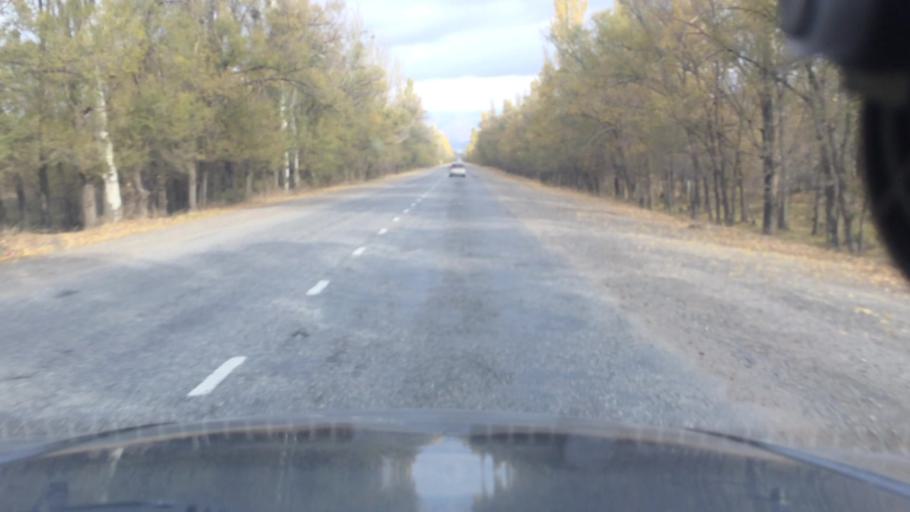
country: KG
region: Ysyk-Koel
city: Tyup
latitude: 42.6297
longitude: 78.3609
